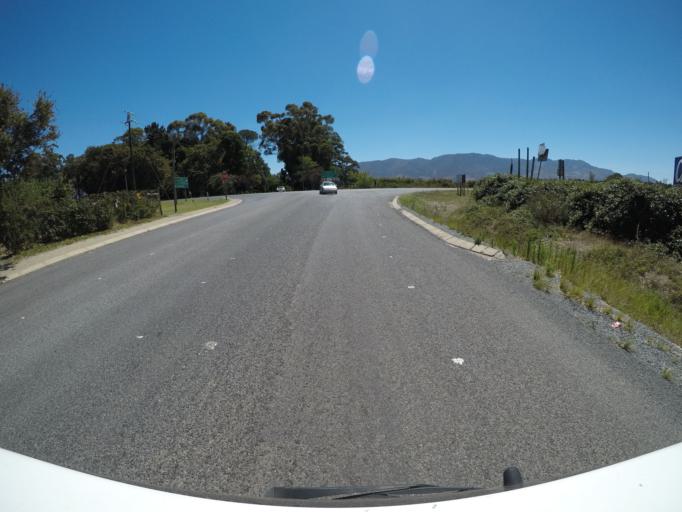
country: ZA
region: Western Cape
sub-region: Overberg District Municipality
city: Grabouw
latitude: -34.1655
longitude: 19.0369
